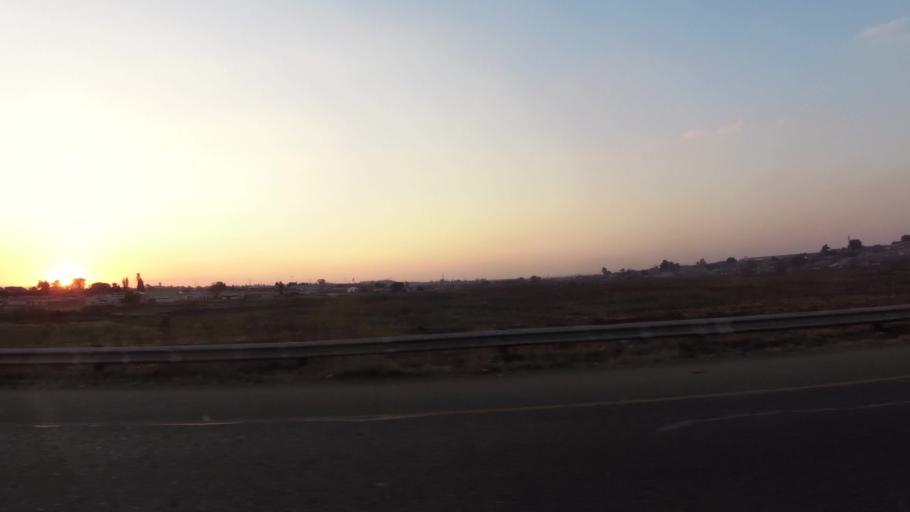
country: ZA
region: Gauteng
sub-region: City of Johannesburg Metropolitan Municipality
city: Soweto
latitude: -26.2903
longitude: 27.8846
